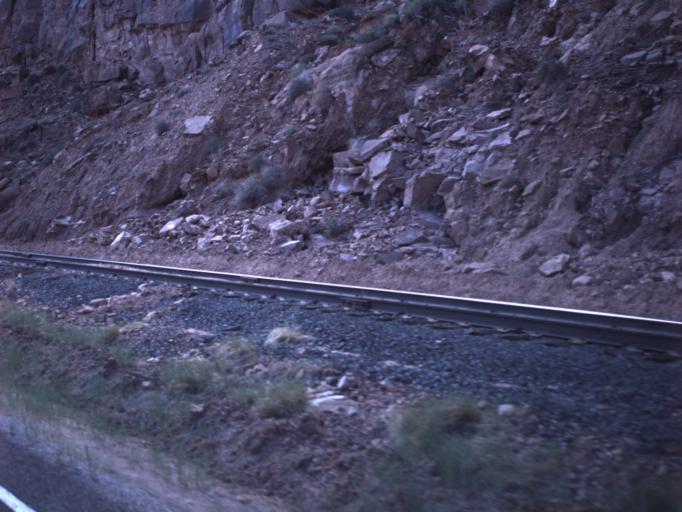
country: US
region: Utah
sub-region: Grand County
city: Moab
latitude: 38.5662
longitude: -109.6588
